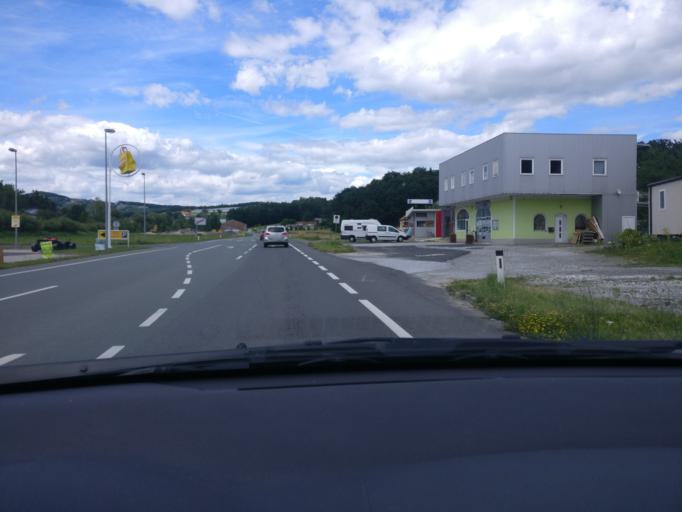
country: AT
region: Styria
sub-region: Politischer Bezirk Weiz
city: Hirnsdorf
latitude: 47.1762
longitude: 15.8094
